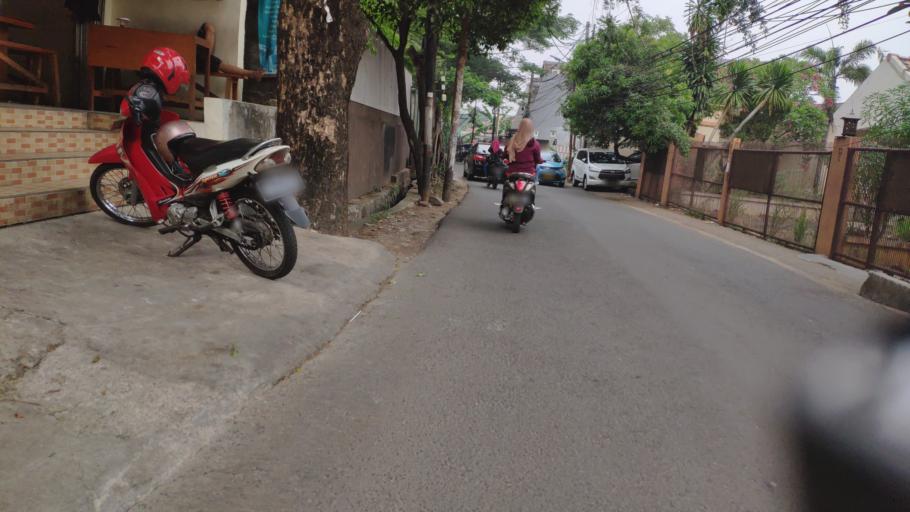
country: ID
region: Jakarta Raya
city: Jakarta
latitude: -6.3008
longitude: 106.8300
